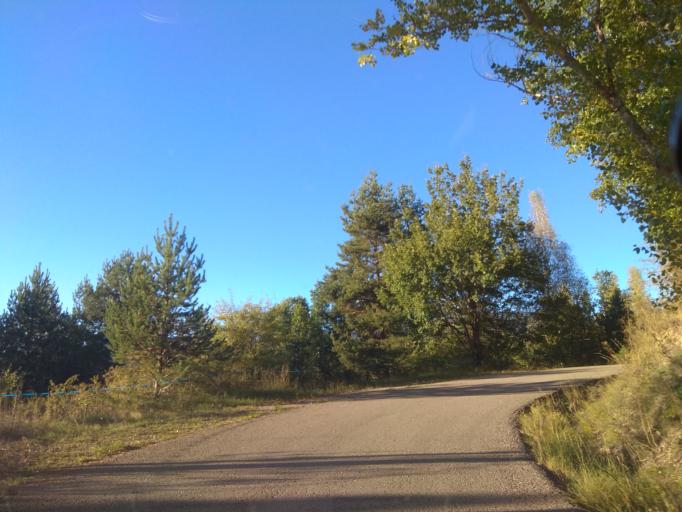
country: ES
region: Catalonia
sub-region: Provincia de Lleida
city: Lles de Cerdanya
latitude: 42.3536
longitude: 1.7267
